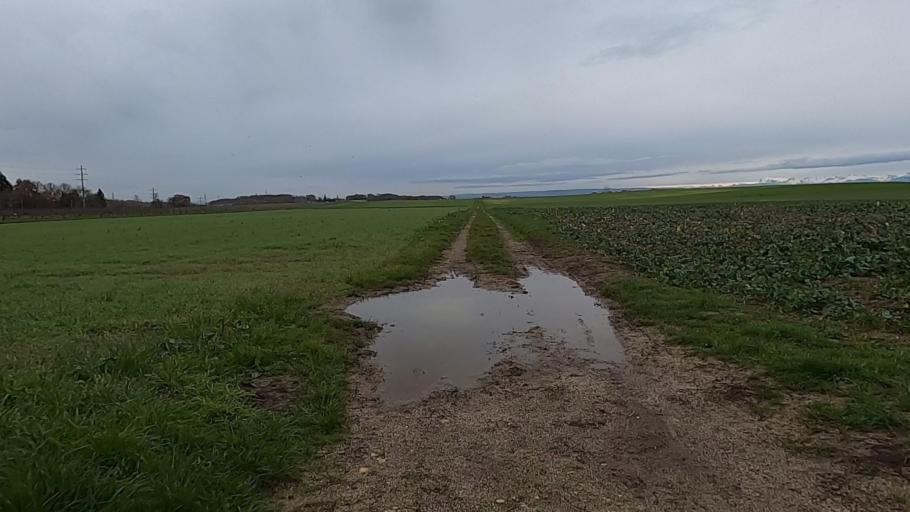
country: CH
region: Vaud
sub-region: Morges District
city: Apples
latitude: 46.5227
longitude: 6.4427
